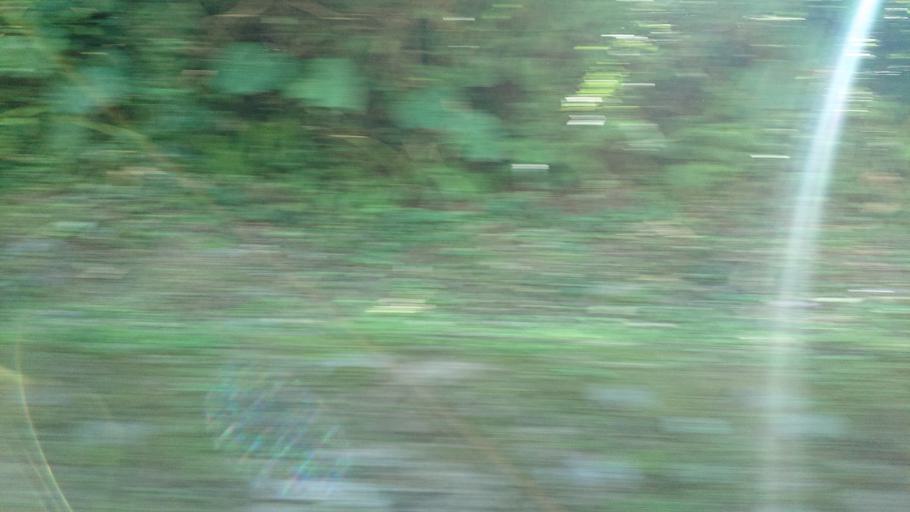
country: TW
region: Taiwan
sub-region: Yilan
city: Yilan
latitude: 24.5777
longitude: 121.4821
